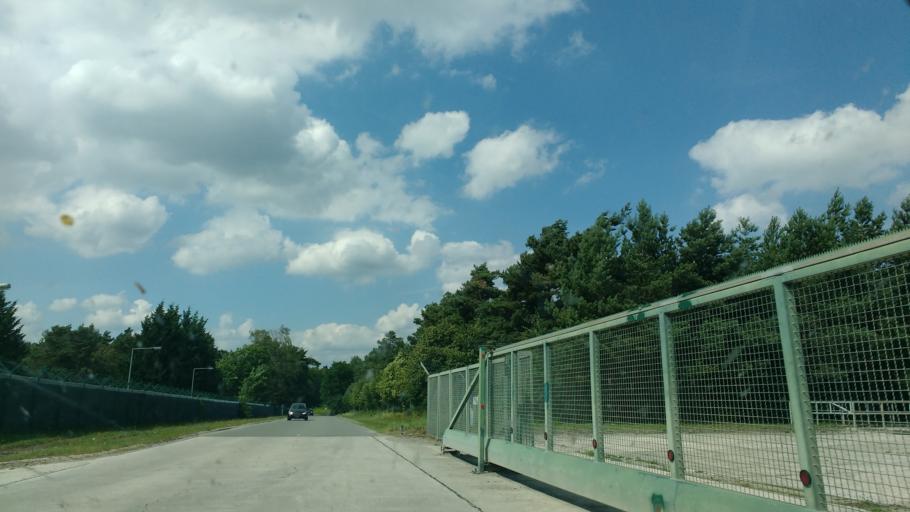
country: DE
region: North Rhine-Westphalia
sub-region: Regierungsbezirk Detmold
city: Paderborn
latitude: 51.7710
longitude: 8.7560
